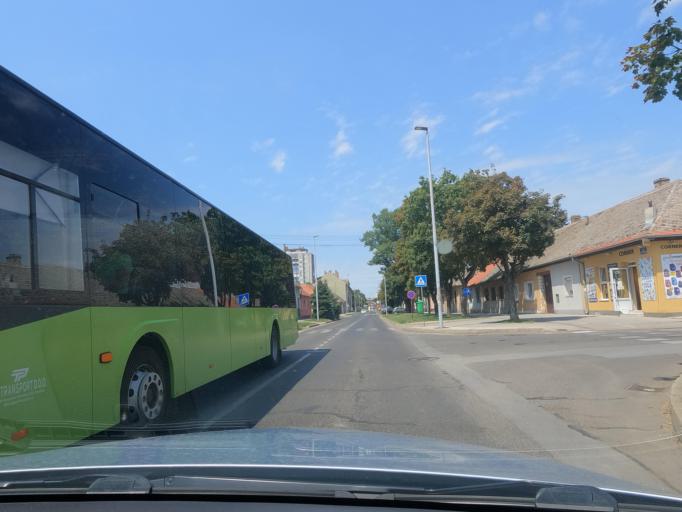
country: RS
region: Autonomna Pokrajina Vojvodina
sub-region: Juznobanatski Okrug
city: Pancevo
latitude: 44.8623
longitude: 20.6474
